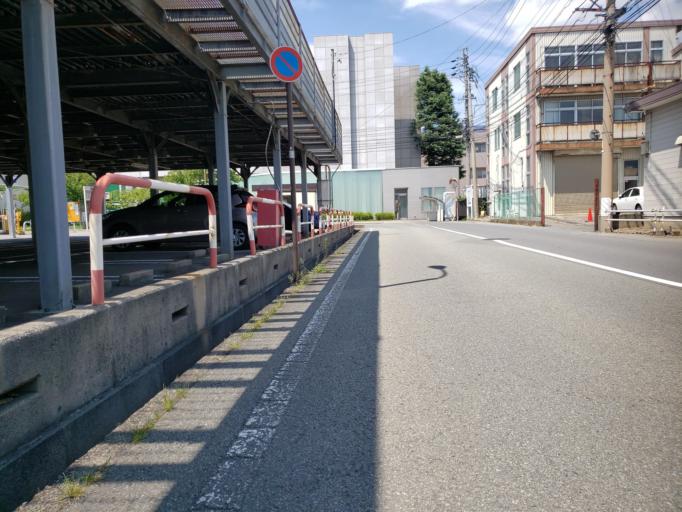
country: JP
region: Nagano
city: Nagano-shi
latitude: 36.6260
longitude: 138.1922
